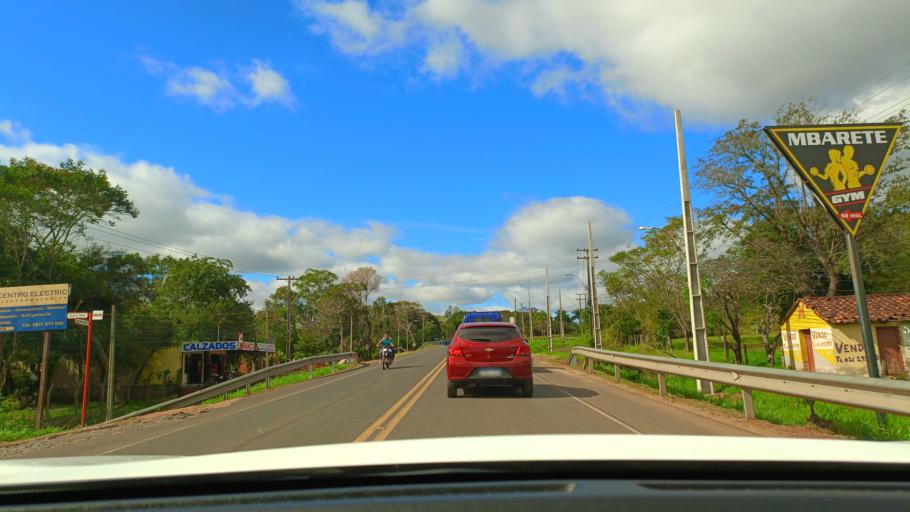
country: PY
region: San Pedro
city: Guayaybi
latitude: -24.6636
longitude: -56.4333
